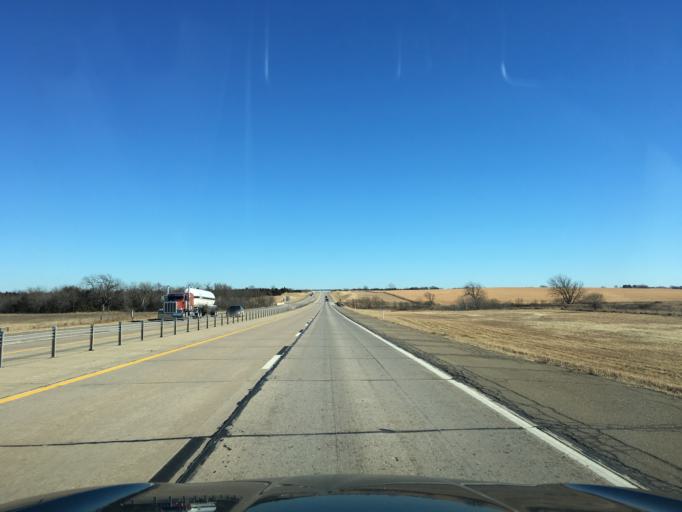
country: US
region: Oklahoma
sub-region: Pawnee County
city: Pawnee
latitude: 36.2251
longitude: -96.8527
